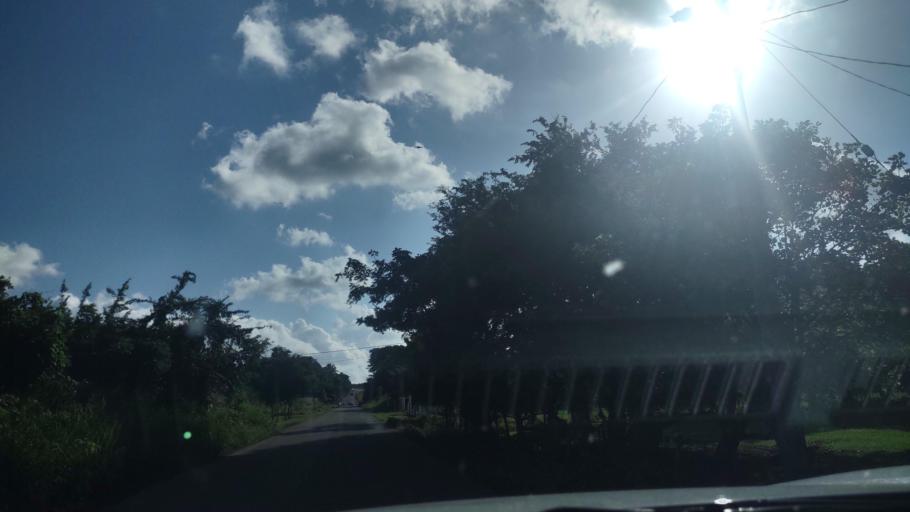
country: MX
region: Veracruz
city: El Tejar
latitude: 19.0678
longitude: -96.1741
